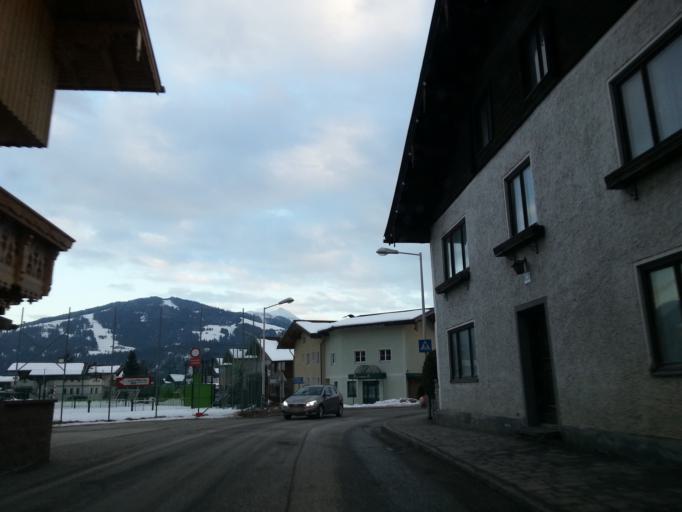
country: AT
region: Salzburg
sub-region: Politischer Bezirk Sankt Johann im Pongau
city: Altenmarkt im Pongau
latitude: 47.3851
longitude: 13.4140
